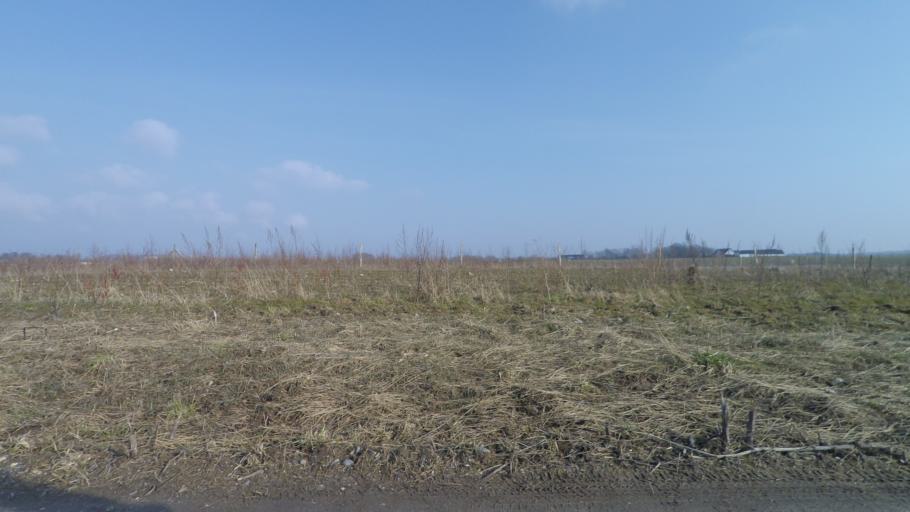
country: DK
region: Central Jutland
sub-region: Arhus Kommune
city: Tranbjerg
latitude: 56.0798
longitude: 10.1353
